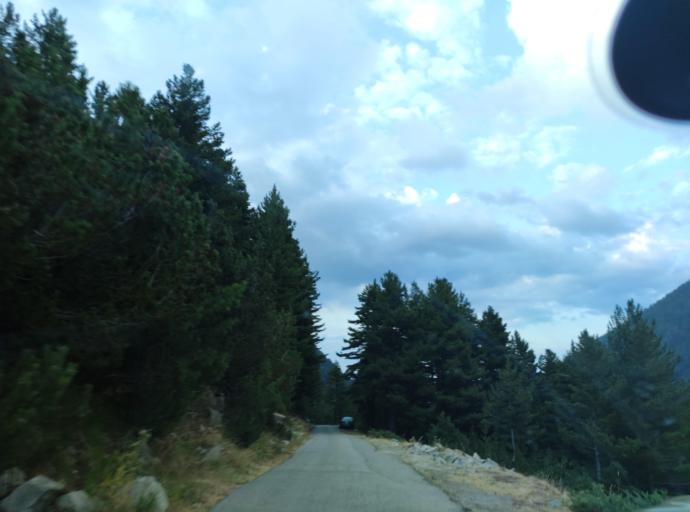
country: BG
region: Blagoevgrad
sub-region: Obshtina Bansko
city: Bansko
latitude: 41.7608
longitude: 23.4169
